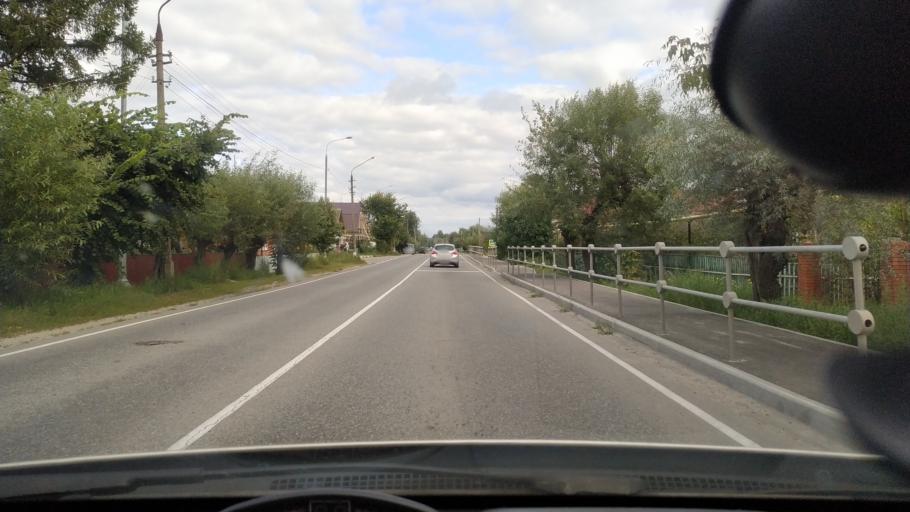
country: RU
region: Moskovskaya
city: Likino-Dulevo
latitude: 55.7300
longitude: 38.9977
